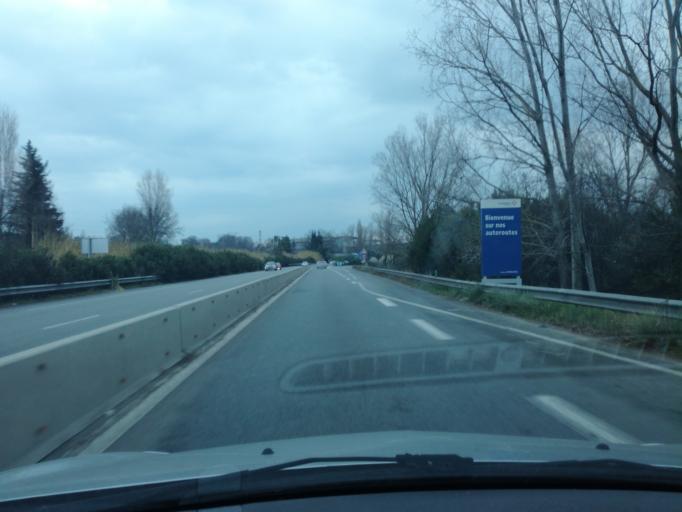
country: FR
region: Provence-Alpes-Cote d'Azur
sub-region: Departement des Alpes-Maritimes
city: Mandelieu-la-Napoule
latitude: 43.5601
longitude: 6.9540
